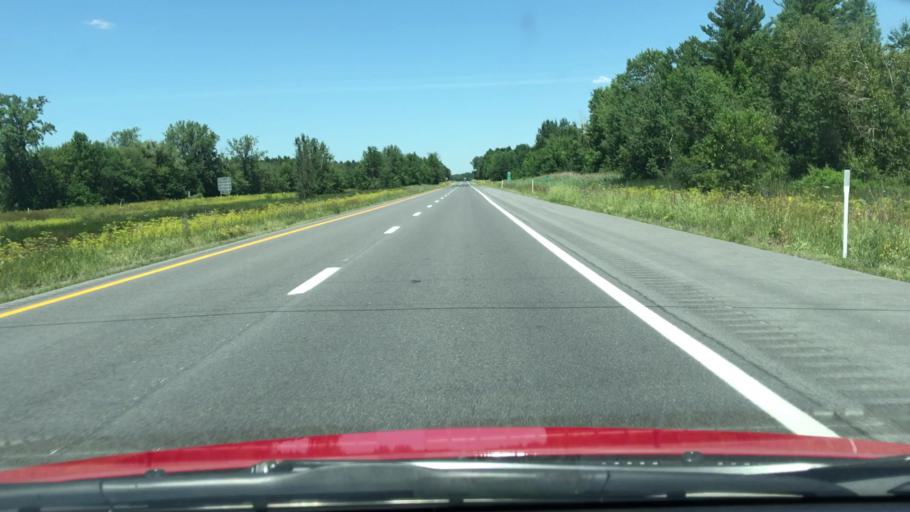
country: US
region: New York
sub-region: Clinton County
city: Cumberland Head
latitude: 44.8229
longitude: -73.4459
